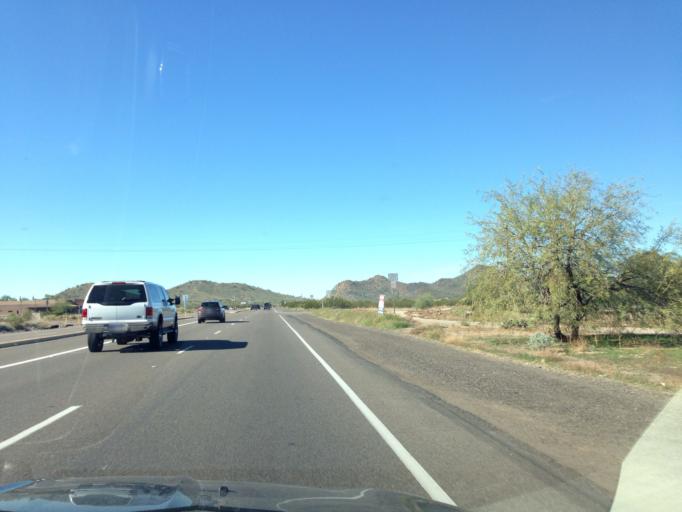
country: US
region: Arizona
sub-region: Maricopa County
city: Anthem
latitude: 33.7992
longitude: -112.0728
